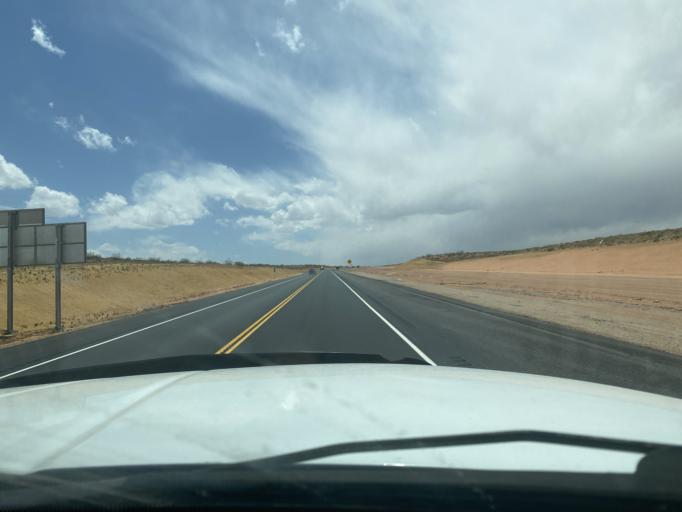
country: US
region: Utah
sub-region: Washington County
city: Hurricane
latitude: 37.1154
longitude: -113.3432
